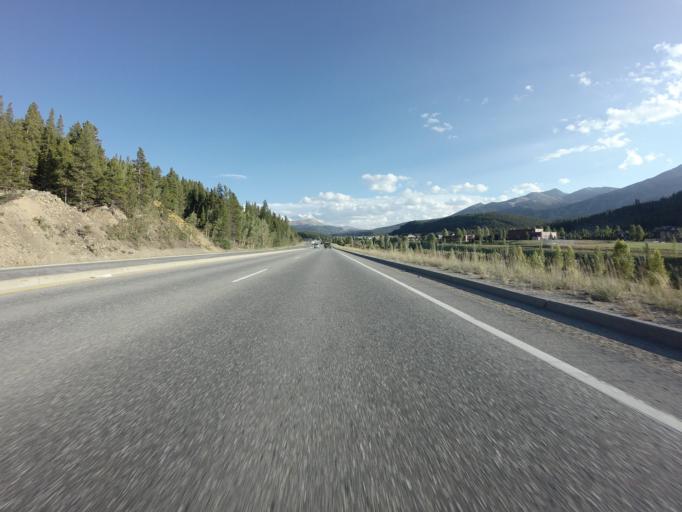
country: US
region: Colorado
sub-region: Summit County
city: Breckenridge
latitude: 39.5028
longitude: -106.0474
